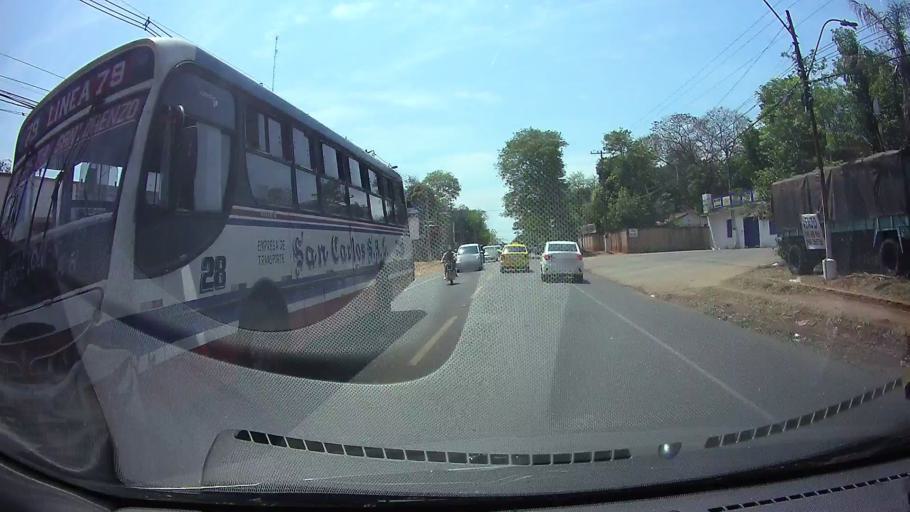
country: PY
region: Central
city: Capiata
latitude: -25.3832
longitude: -57.4732
